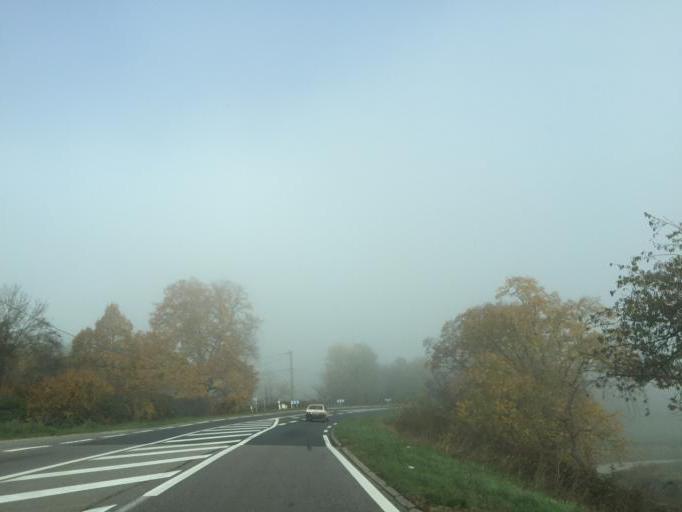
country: FR
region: Rhone-Alpes
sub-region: Departement du Rhone
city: Montagny
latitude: 45.6464
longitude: 4.7463
